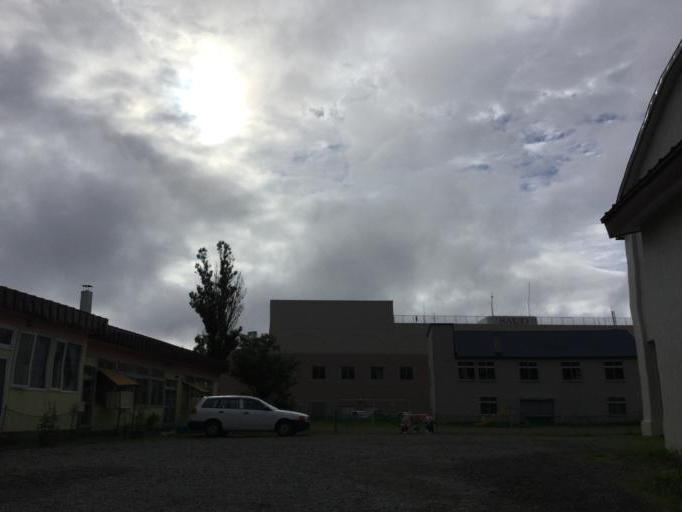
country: JP
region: Hokkaido
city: Wakkanai
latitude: 45.3982
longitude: 141.6906
